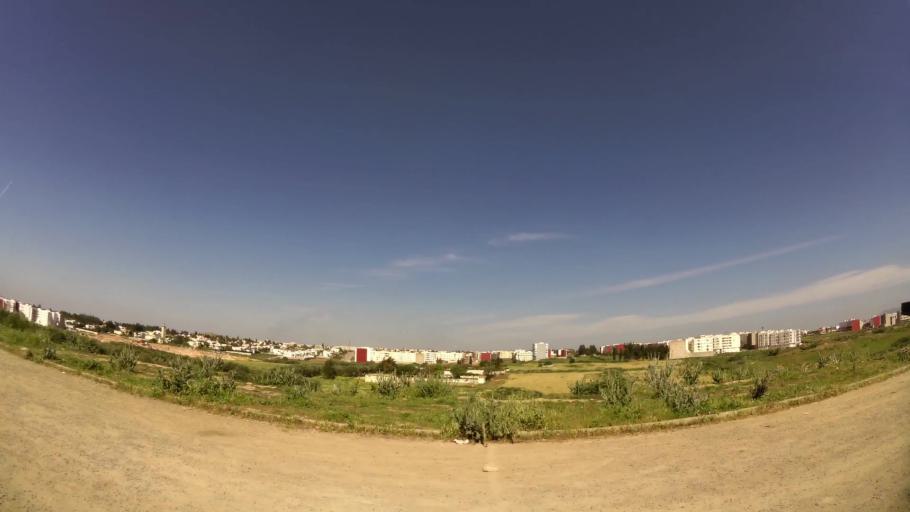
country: MA
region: Fes-Boulemane
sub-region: Fes
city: Fes
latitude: 33.9994
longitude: -5.0034
